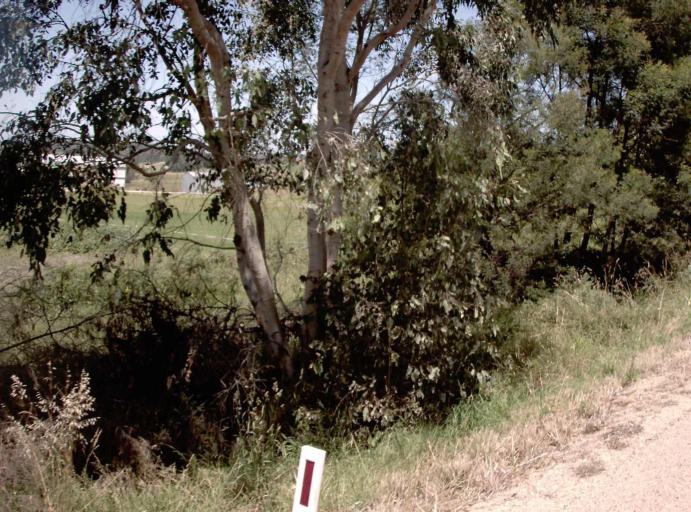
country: AU
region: Victoria
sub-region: East Gippsland
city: Bairnsdale
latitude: -37.7226
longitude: 147.8034
